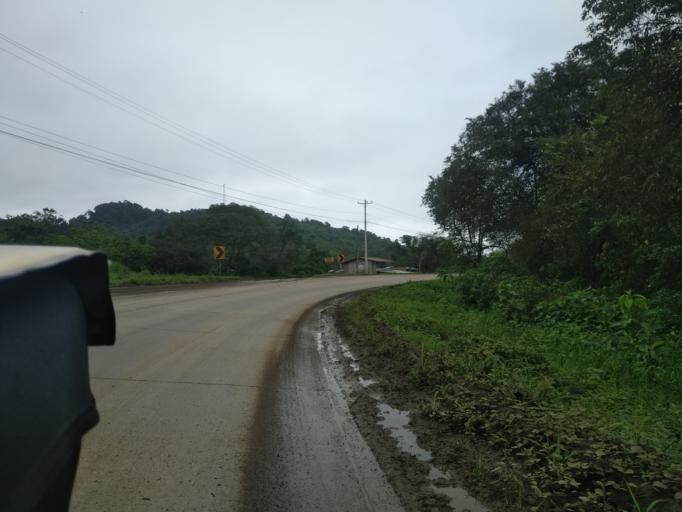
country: EC
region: Manabi
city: Jipijapa
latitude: -1.6709
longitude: -80.8080
